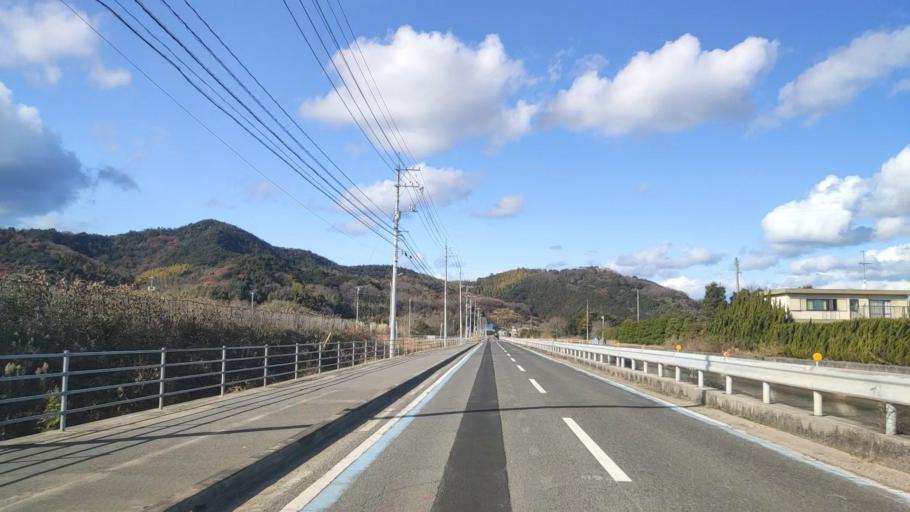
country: JP
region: Hiroshima
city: Innoshima
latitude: 34.2140
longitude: 133.1092
